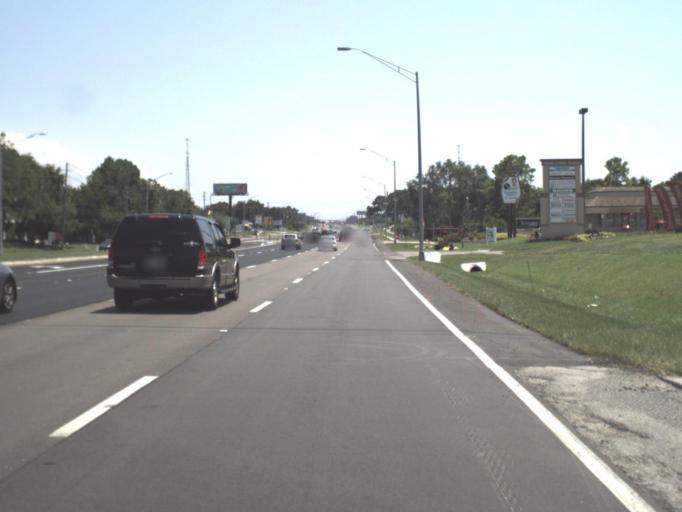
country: US
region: Florida
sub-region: Pinellas County
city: Saint George
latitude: 28.0627
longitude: -82.7391
